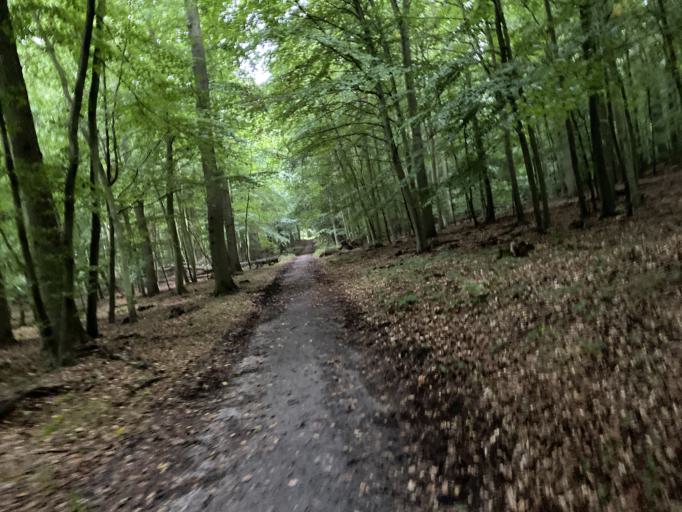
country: DE
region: Mecklenburg-Vorpommern
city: Ostseebad Binz
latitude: 54.4482
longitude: 13.5508
